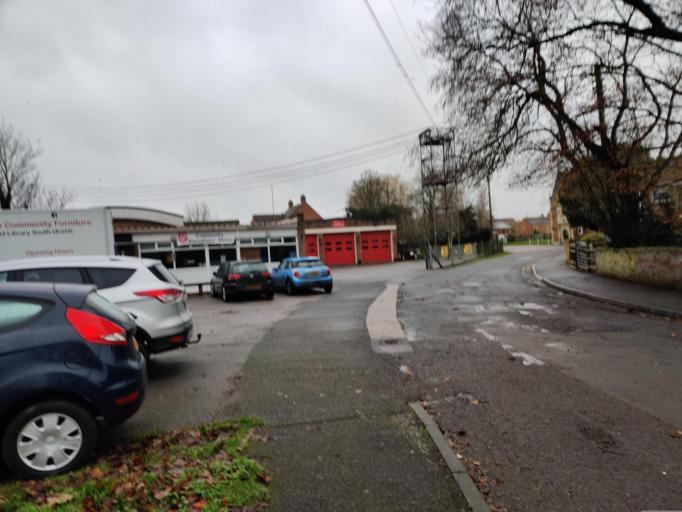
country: GB
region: England
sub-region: Lincolnshire
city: Bourne
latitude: 52.7656
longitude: -0.3763
